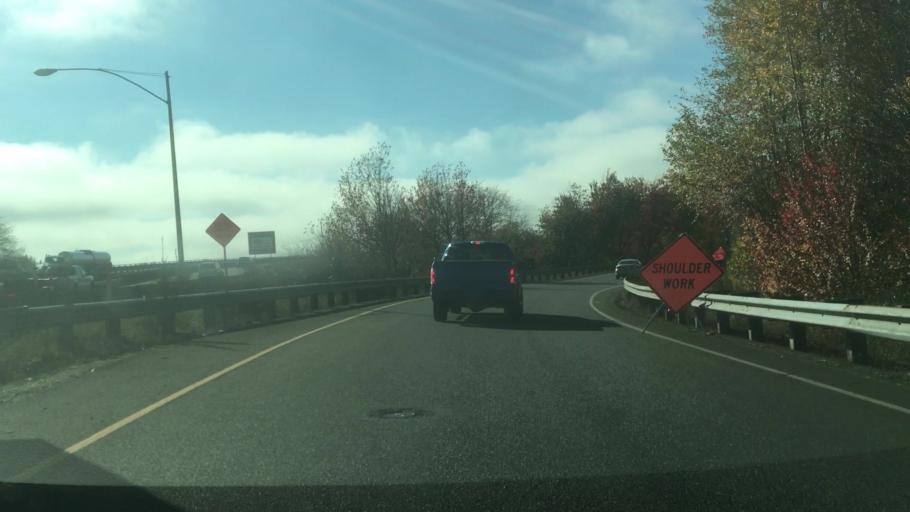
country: US
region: Washington
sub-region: Grays Harbor County
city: Montesano
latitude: 46.9773
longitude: -123.5970
